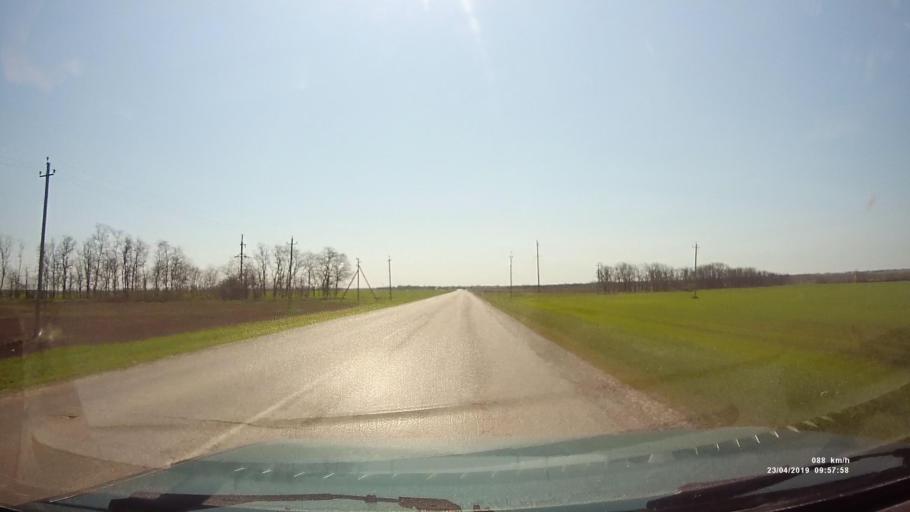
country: RU
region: Rostov
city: Sovetskoye
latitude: 46.7834
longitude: 42.0928
